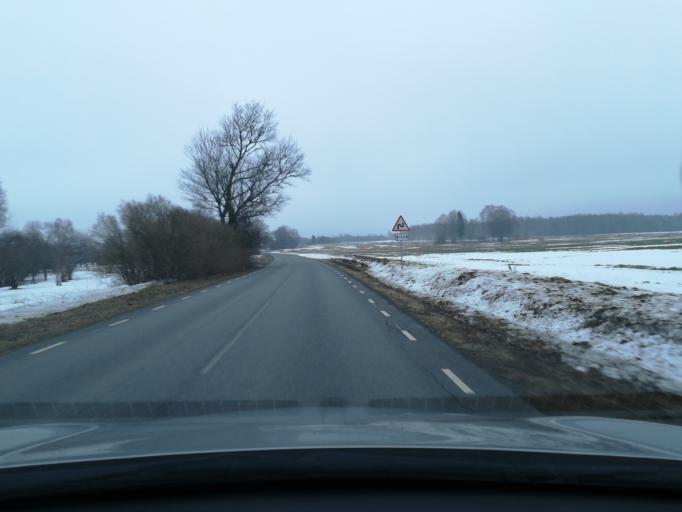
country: EE
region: Harju
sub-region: Kuusalu vald
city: Kuusalu
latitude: 59.4698
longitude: 25.5249
